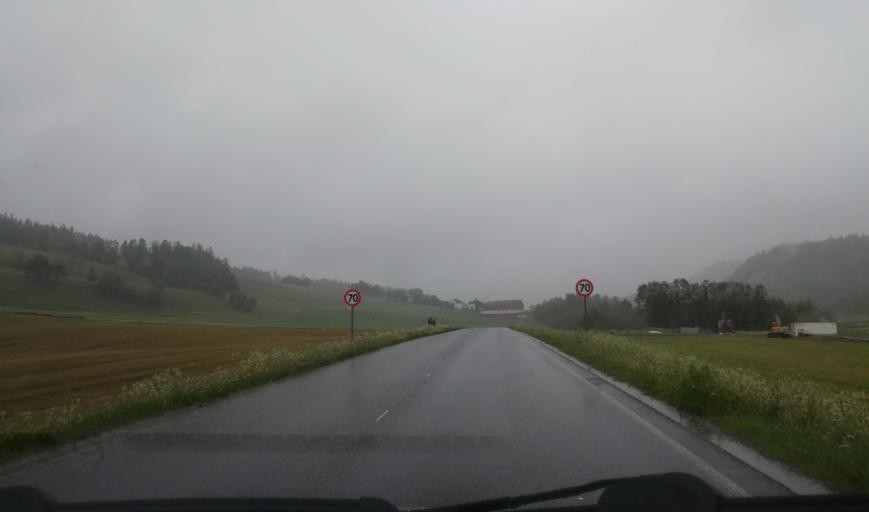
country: NO
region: Nord-Trondelag
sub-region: Stjordal
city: Stjordalshalsen
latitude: 63.3919
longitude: 10.9817
